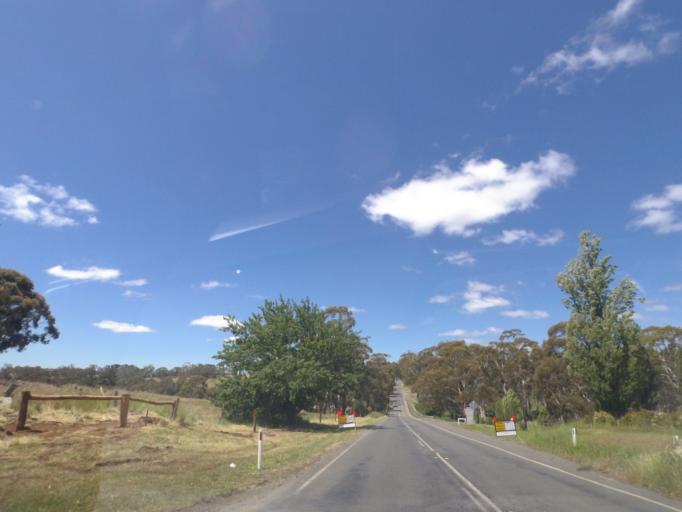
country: AU
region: Victoria
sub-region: Mount Alexander
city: Castlemaine
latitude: -37.2932
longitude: 144.2456
